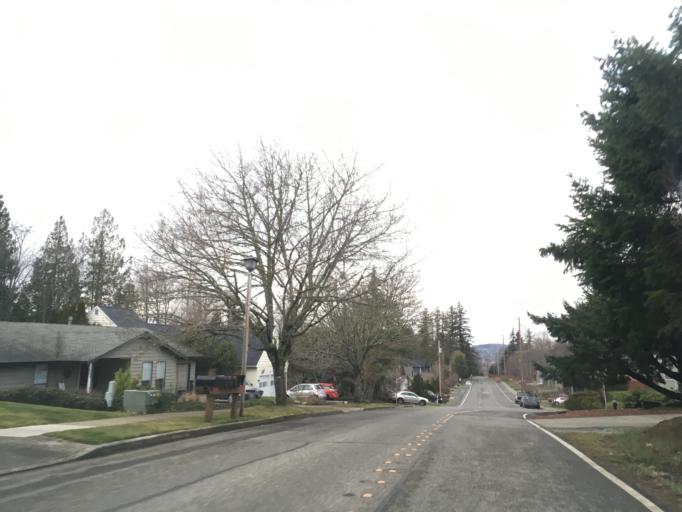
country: US
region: Washington
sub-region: Whatcom County
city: Bellingham
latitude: 48.7275
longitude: -122.4644
